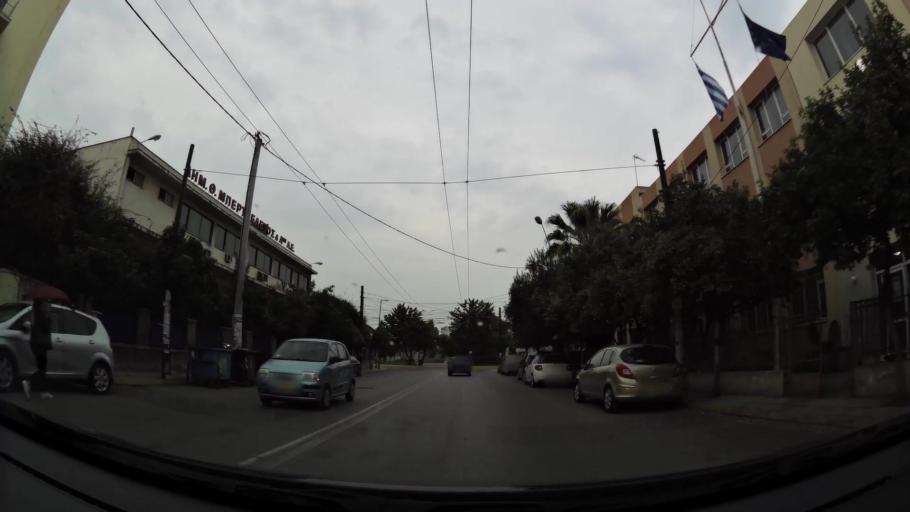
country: GR
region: Attica
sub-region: Nomos Piraios
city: Agios Ioannis Rentis
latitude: 37.9566
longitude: 23.6705
